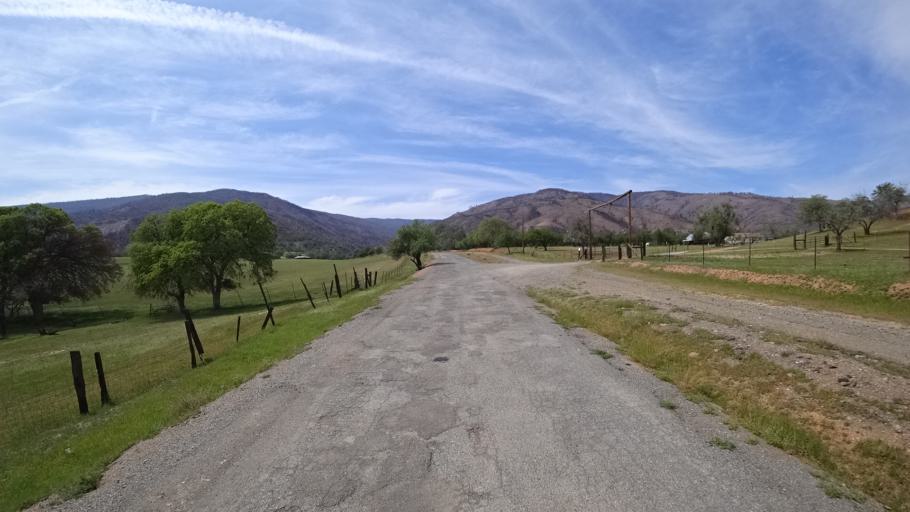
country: US
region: California
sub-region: Glenn County
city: Willows
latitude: 39.5763
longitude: -122.6061
